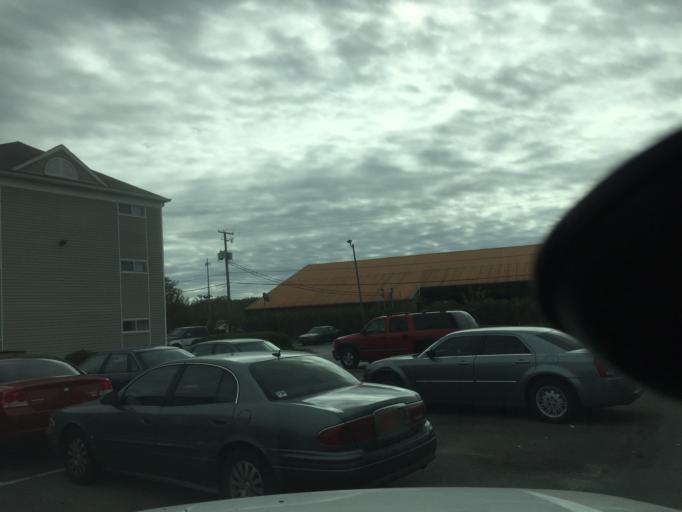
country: US
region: Georgia
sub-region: Chatham County
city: Garden City
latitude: 32.1260
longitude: -81.1688
